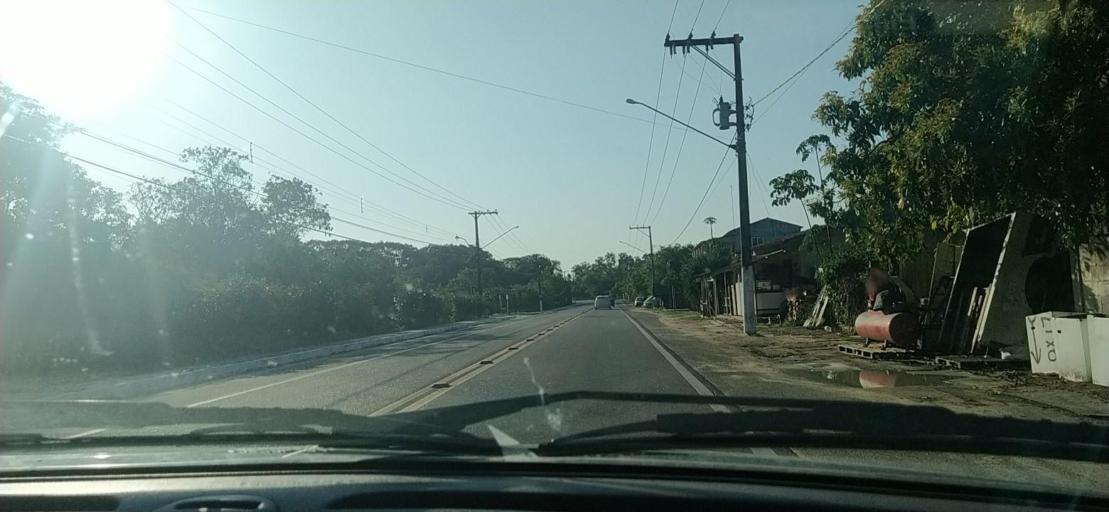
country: BR
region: Espirito Santo
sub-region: Conceicao Da Barra
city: Conceicao da Barra
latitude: -18.5687
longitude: -39.7420
